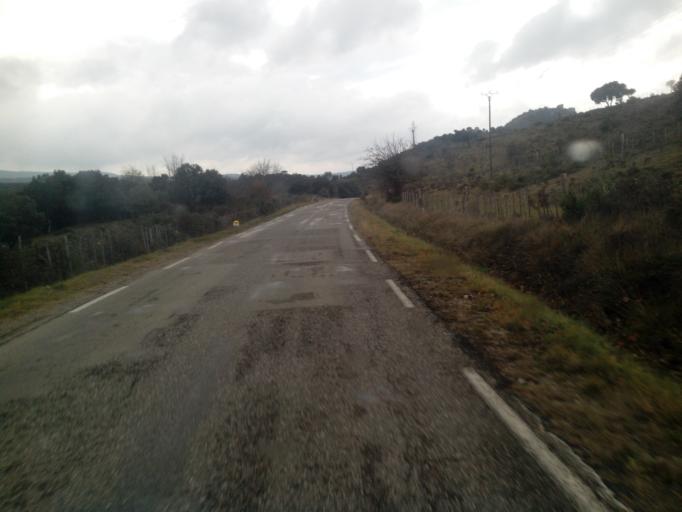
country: FR
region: Languedoc-Roussillon
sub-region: Departement du Gard
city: Saint-Hippolyte-du-Fort
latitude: 43.9464
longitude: 3.8074
